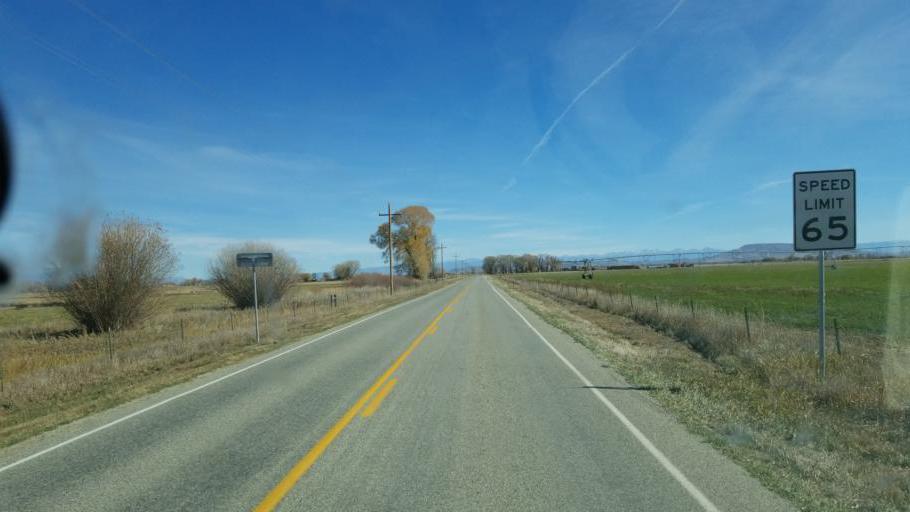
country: US
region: Colorado
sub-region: Conejos County
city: Conejos
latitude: 37.2837
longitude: -106.0370
